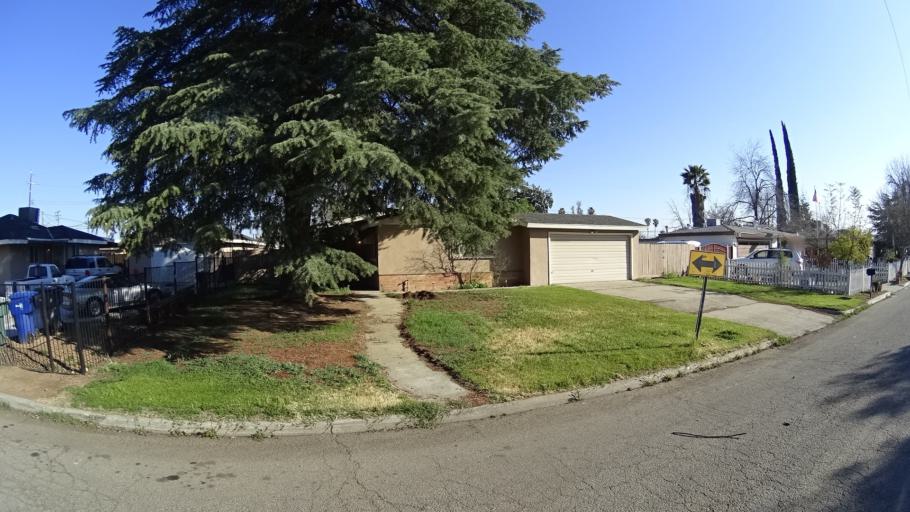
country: US
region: California
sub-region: Fresno County
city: Fresno
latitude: 36.8239
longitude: -119.7885
